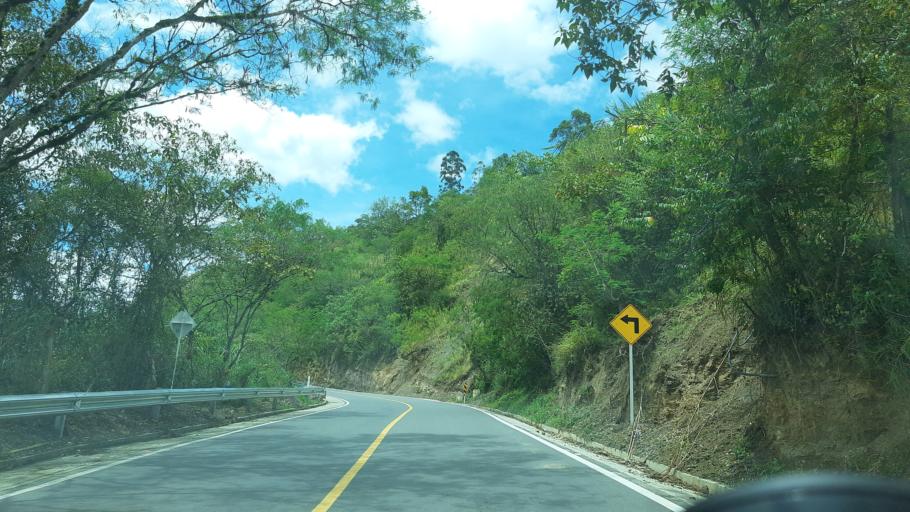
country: CO
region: Boyaca
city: Somondoco
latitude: 5.0082
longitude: -73.4403
